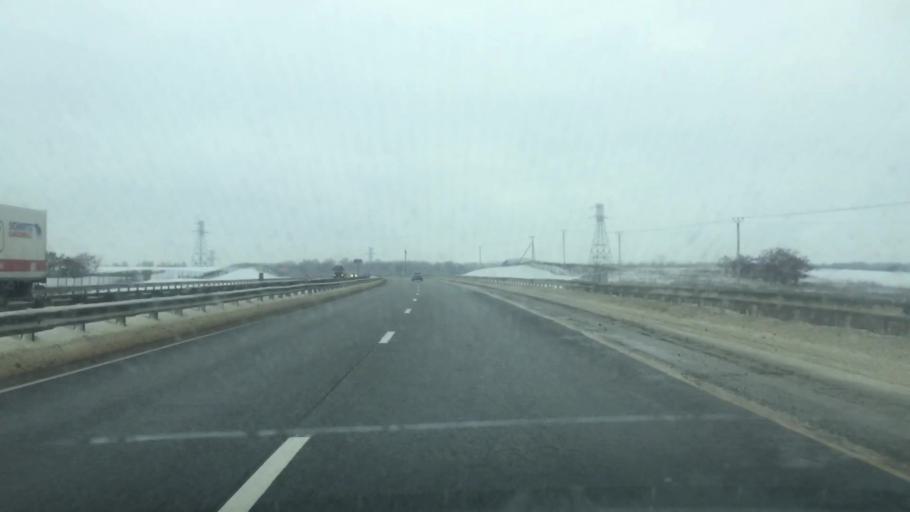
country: RU
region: Tula
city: Yefremov
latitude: 53.1009
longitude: 38.1764
